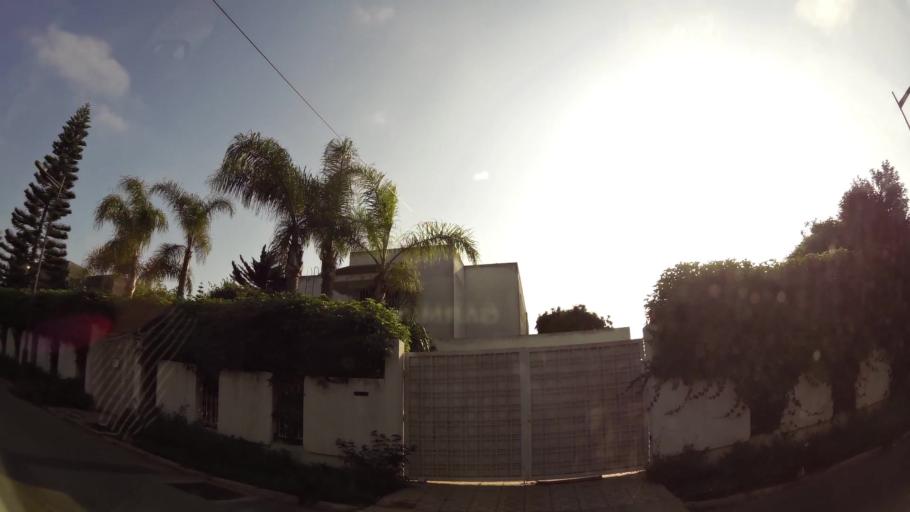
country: MA
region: Rabat-Sale-Zemmour-Zaer
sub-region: Rabat
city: Rabat
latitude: 33.9433
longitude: -6.8125
